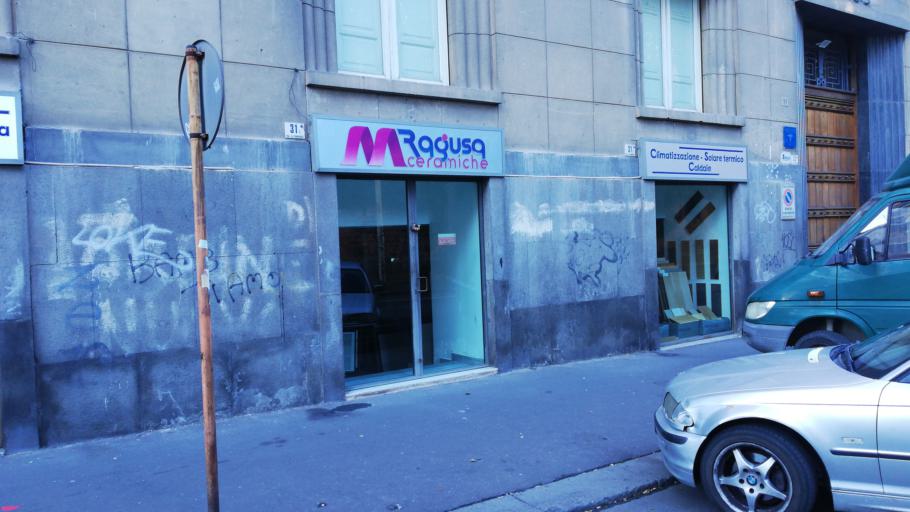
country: IT
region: Sicily
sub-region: Catania
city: Canalicchio
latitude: 37.5172
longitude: 15.0896
